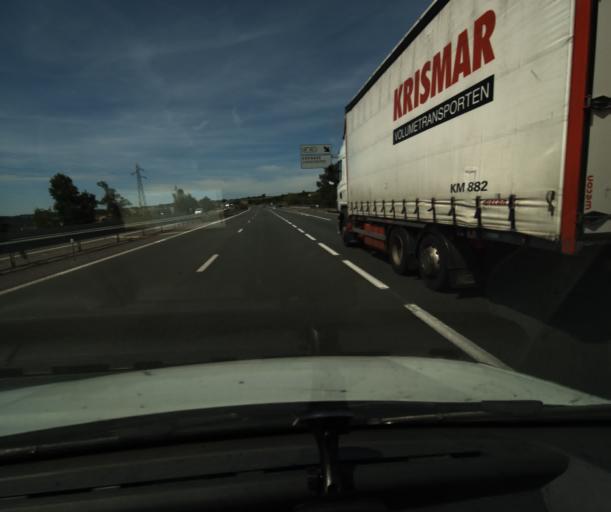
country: FR
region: Midi-Pyrenees
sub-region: Departement de la Haute-Garonne
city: Saint-Sauveur
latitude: 43.7630
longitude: 1.3857
